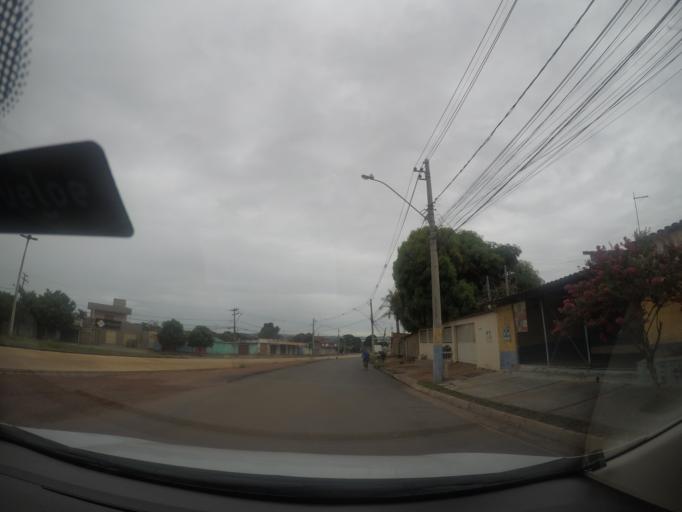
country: BR
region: Goias
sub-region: Goiania
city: Goiania
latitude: -16.6169
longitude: -49.2972
